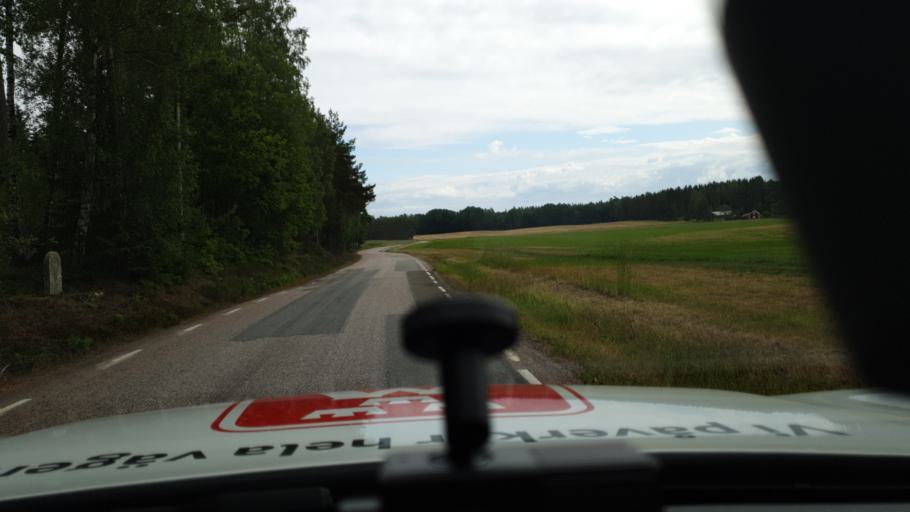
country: SE
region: Vaestra Goetaland
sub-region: Karlsborgs Kommun
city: Molltorp
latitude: 58.4309
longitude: 14.3807
